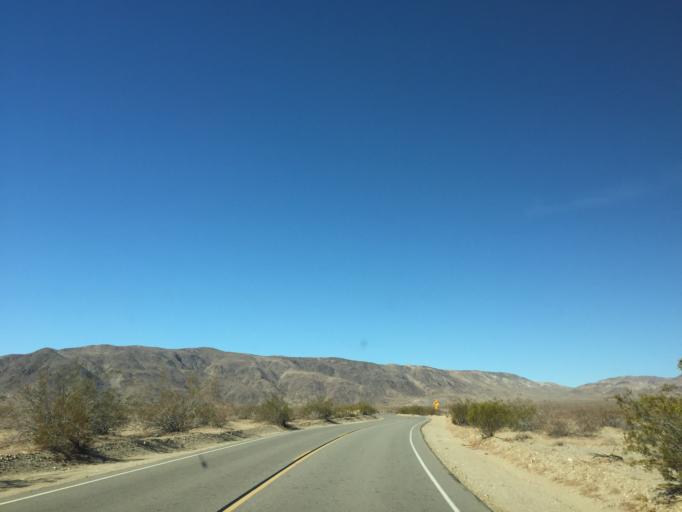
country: US
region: California
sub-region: San Bernardino County
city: Twentynine Palms
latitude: 33.9165
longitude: -115.8789
